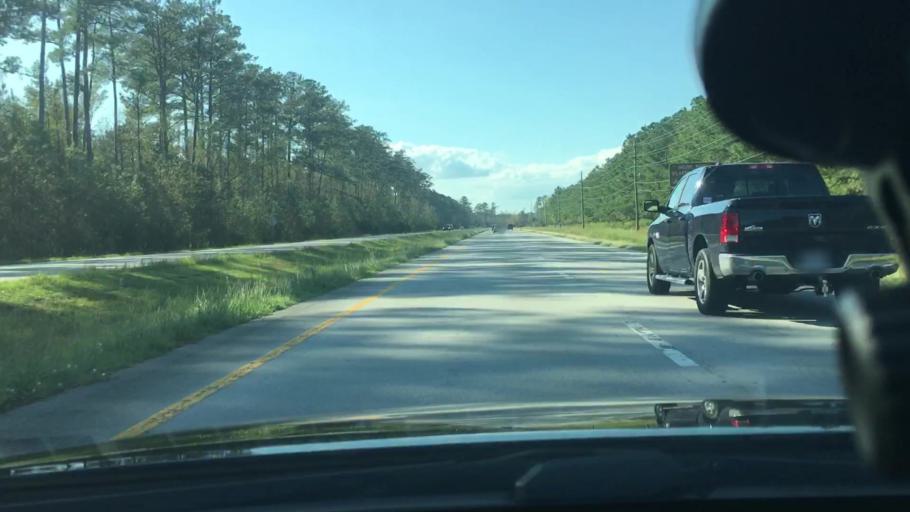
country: US
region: North Carolina
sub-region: Craven County
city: Neuse Forest
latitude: 34.9641
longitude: -76.9587
